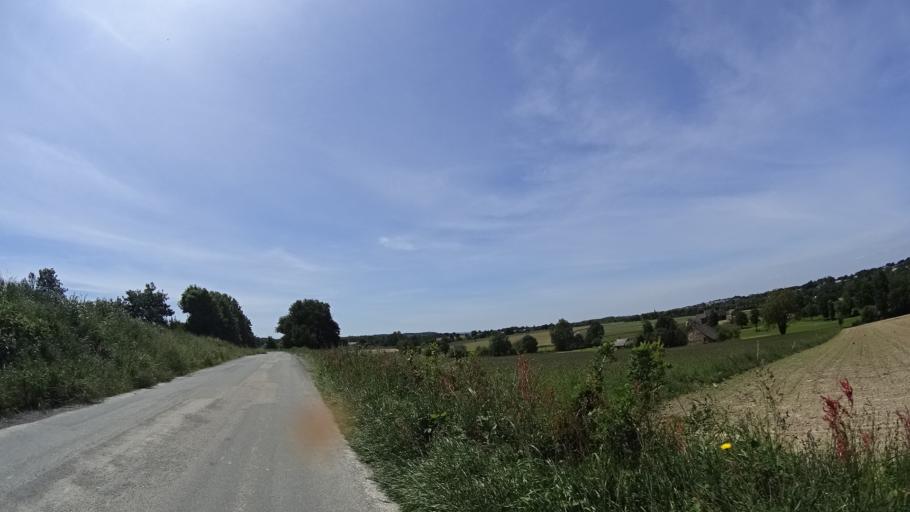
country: FR
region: Brittany
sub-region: Departement d'Ille-et-Vilaine
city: Iffendic
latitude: 48.1316
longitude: -1.9969
